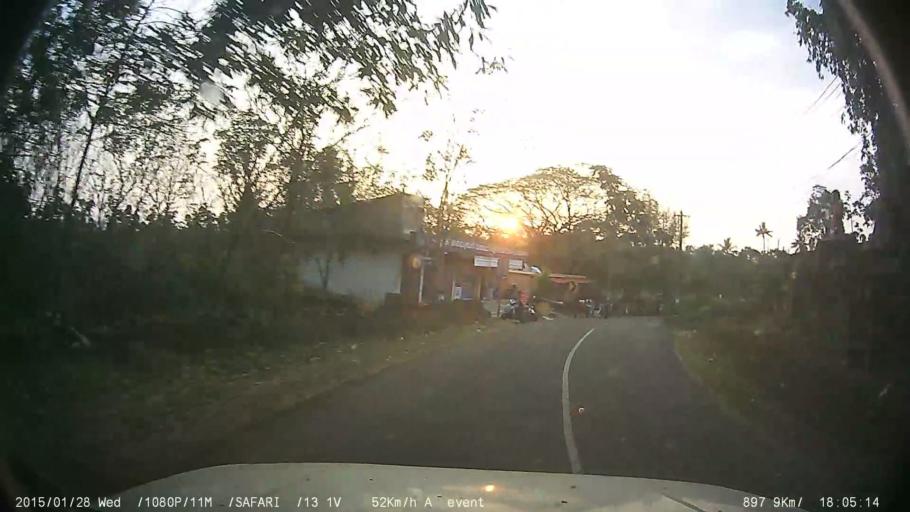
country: IN
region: Kerala
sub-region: Kottayam
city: Palackattumala
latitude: 9.7255
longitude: 76.5802
